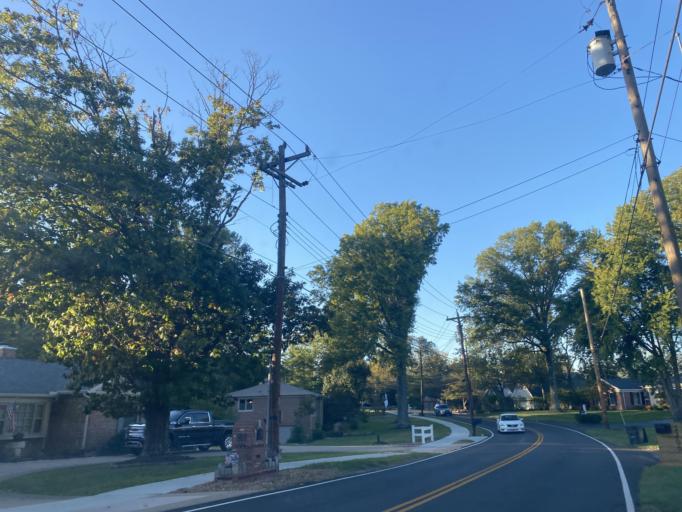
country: US
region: Kentucky
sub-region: Campbell County
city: Dayton
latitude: 39.1044
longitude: -84.4514
